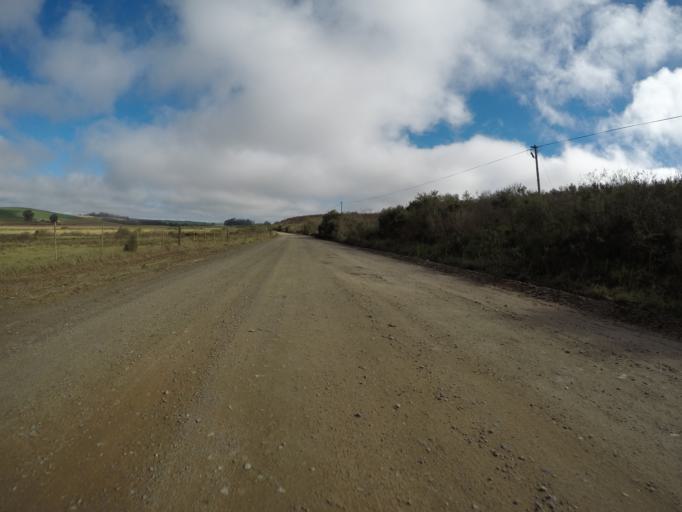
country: ZA
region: Western Cape
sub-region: Cape Winelands District Municipality
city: Ashton
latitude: -34.1223
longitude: 19.8350
